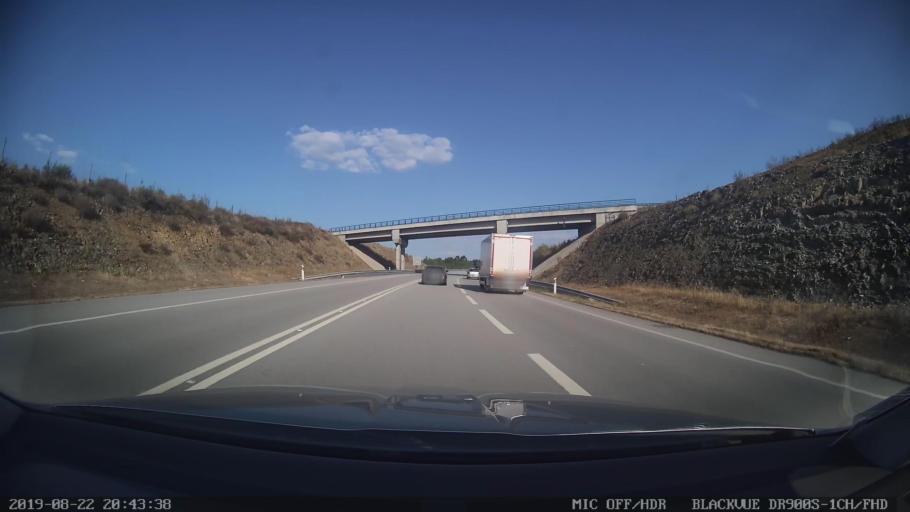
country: PT
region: Castelo Branco
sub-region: Proenca-A-Nova
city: Proenca-a-Nova
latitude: 39.7000
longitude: -7.8356
